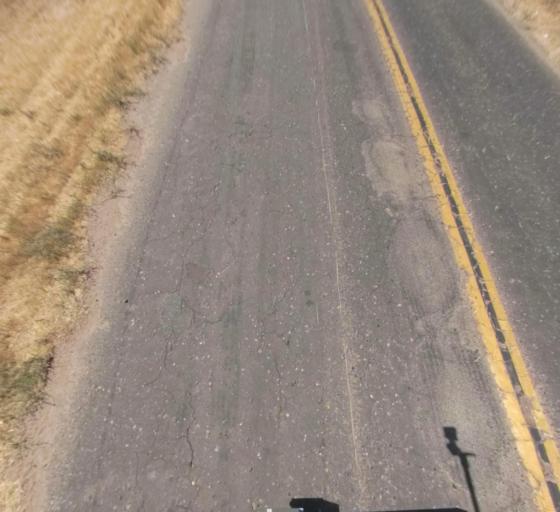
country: US
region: California
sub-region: Madera County
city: Parksdale
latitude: 36.9151
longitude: -119.9651
